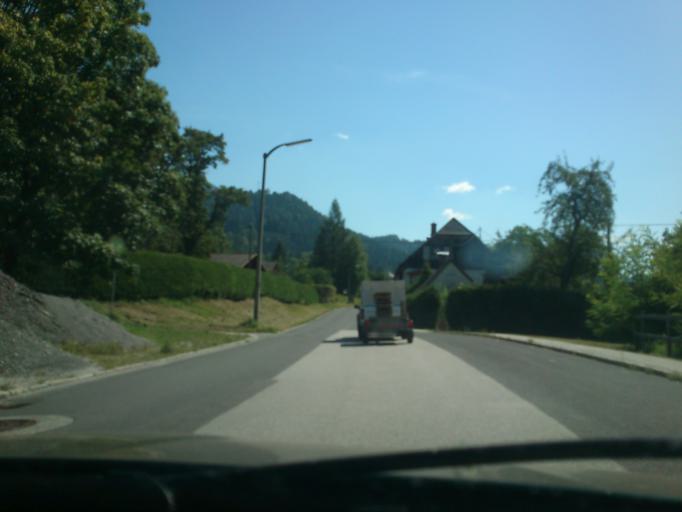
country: AT
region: Upper Austria
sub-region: Politischer Bezirk Kirchdorf an der Krems
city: Rossleithen
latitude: 47.7224
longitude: 14.3211
